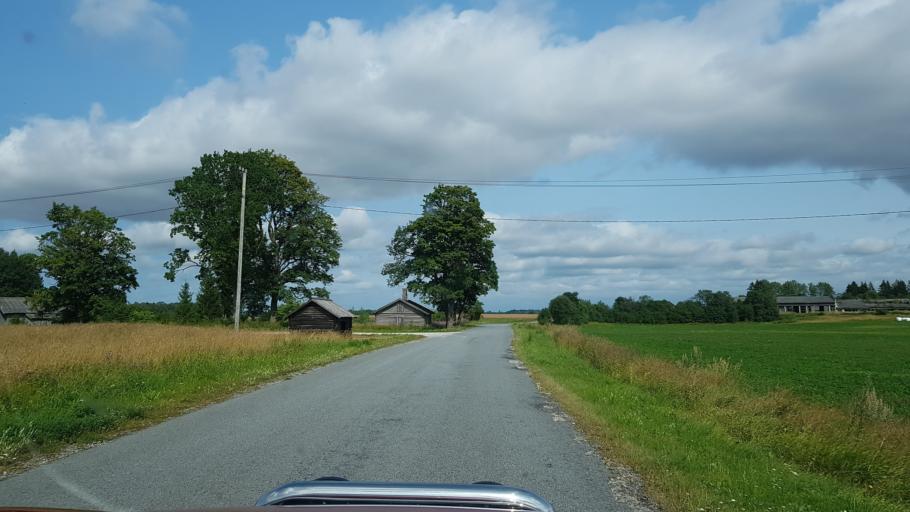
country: EE
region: Laeaene-Virumaa
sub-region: Kadrina vald
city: Kadrina
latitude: 59.3375
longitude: 26.0526
